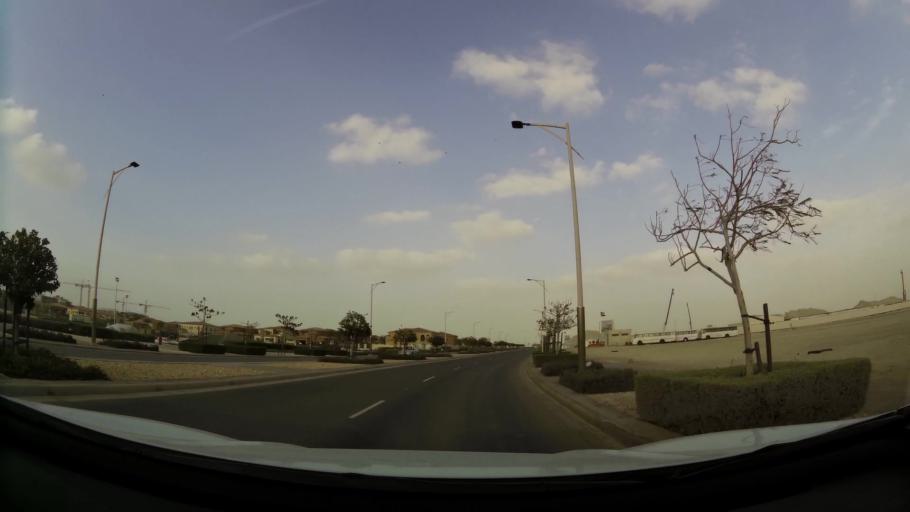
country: AE
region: Abu Dhabi
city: Abu Dhabi
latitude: 24.5549
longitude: 54.4532
